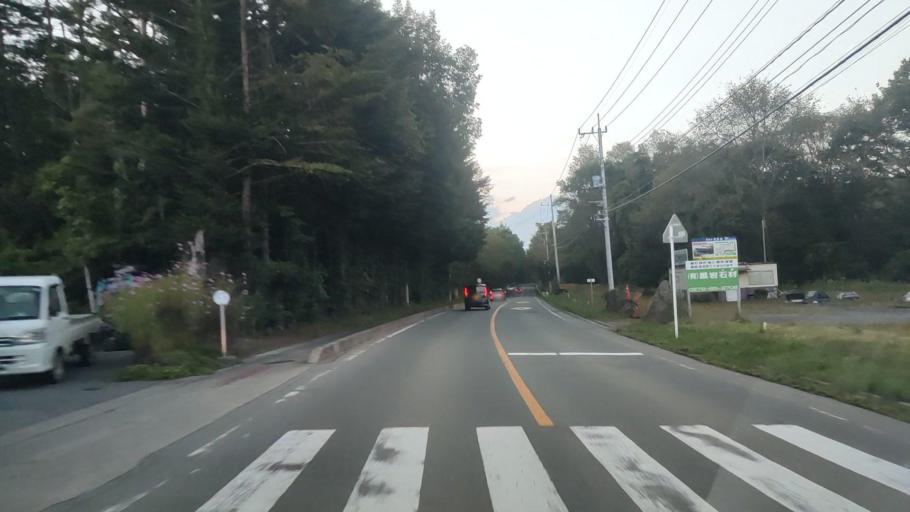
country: JP
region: Nagano
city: Komoro
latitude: 36.4883
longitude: 138.5823
